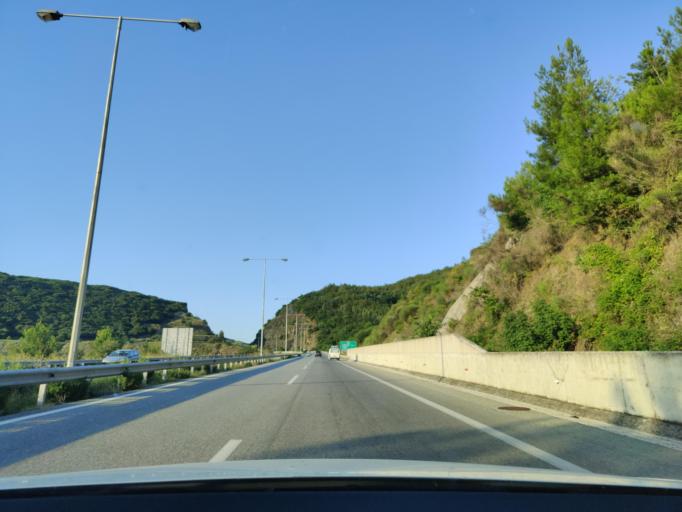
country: GR
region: East Macedonia and Thrace
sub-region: Nomos Kavalas
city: Amygdaleonas
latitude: 40.9504
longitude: 24.3779
